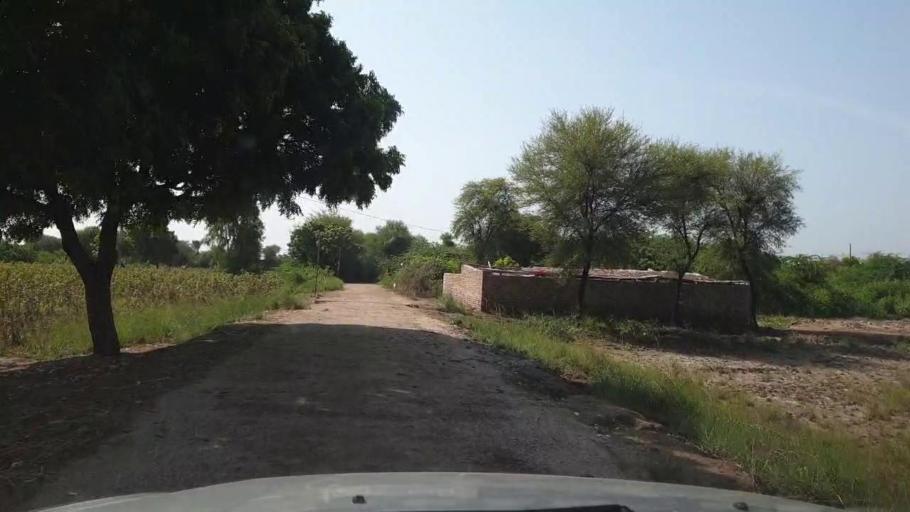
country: PK
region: Sindh
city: Tando Ghulam Ali
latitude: 25.1323
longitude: 68.8714
